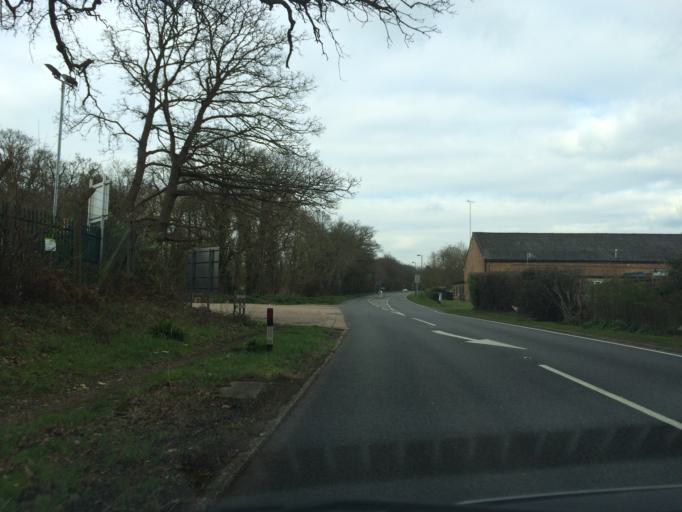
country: GB
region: England
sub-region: Surrey
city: Woking
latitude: 51.3511
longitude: -0.5641
